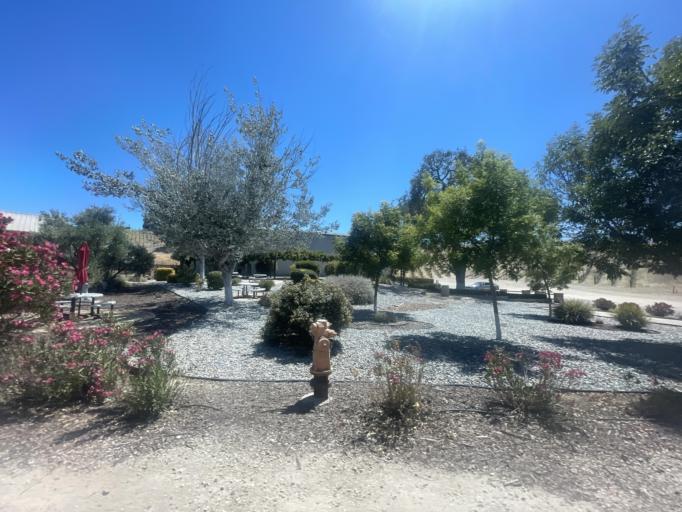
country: US
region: California
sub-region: San Luis Obispo County
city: Paso Robles
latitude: 35.6579
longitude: -120.5455
